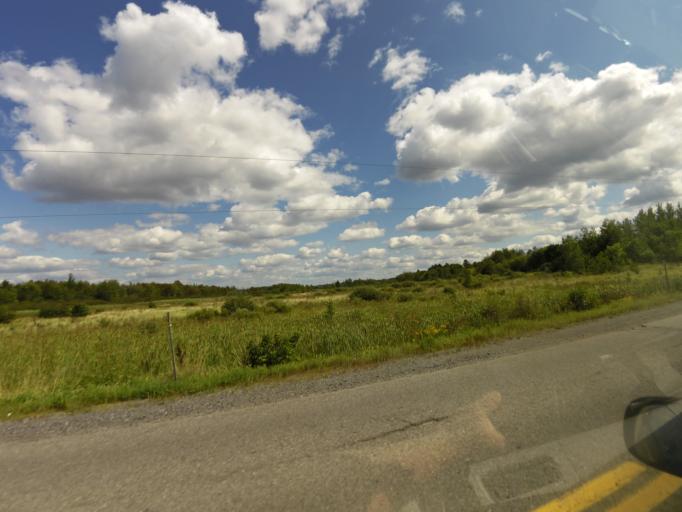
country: CA
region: Ontario
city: Ottawa
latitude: 45.3947
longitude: -75.5530
